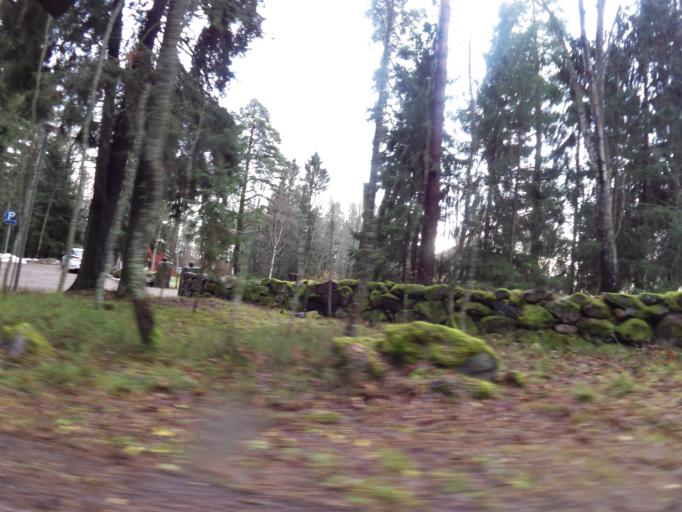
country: FI
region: Uusimaa
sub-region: Helsinki
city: Teekkarikylae
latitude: 60.2022
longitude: 24.8222
